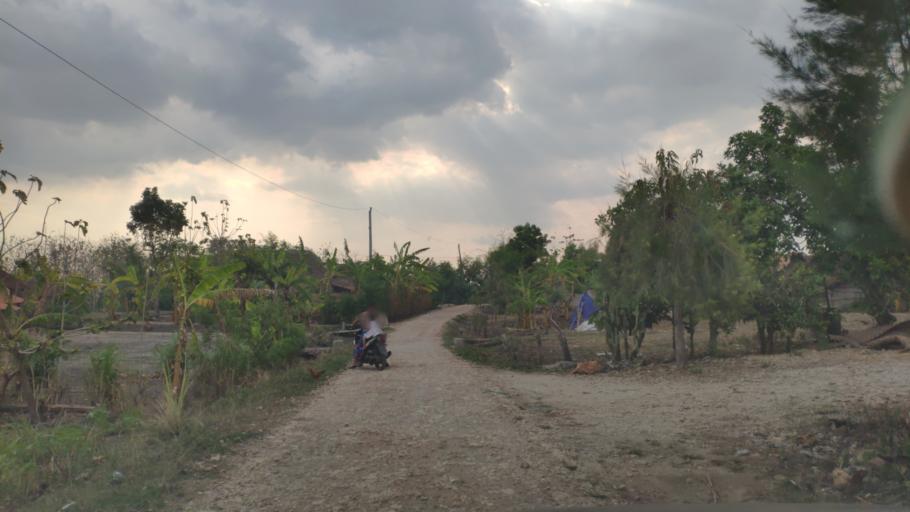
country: ID
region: Central Java
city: Randublatung
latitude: -7.2854
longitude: 111.2783
